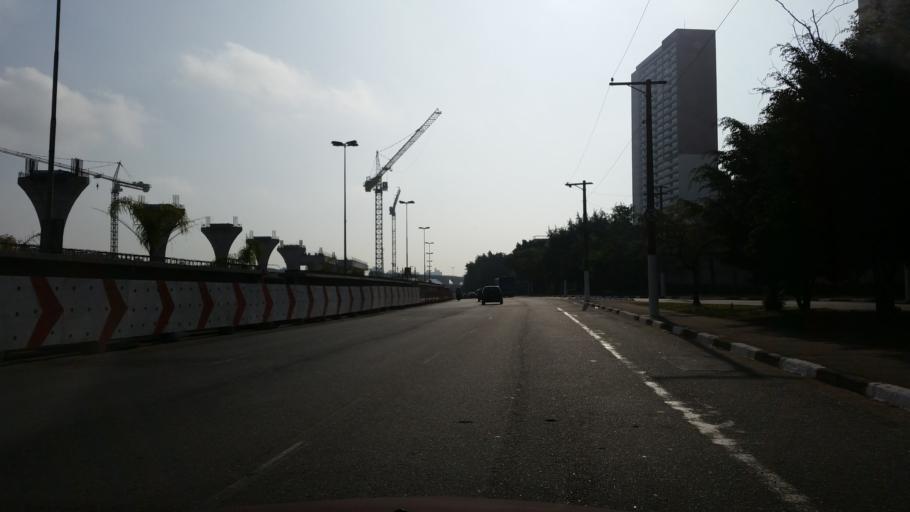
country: BR
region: Sao Paulo
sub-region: Diadema
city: Diadema
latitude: -23.6360
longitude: -46.6652
